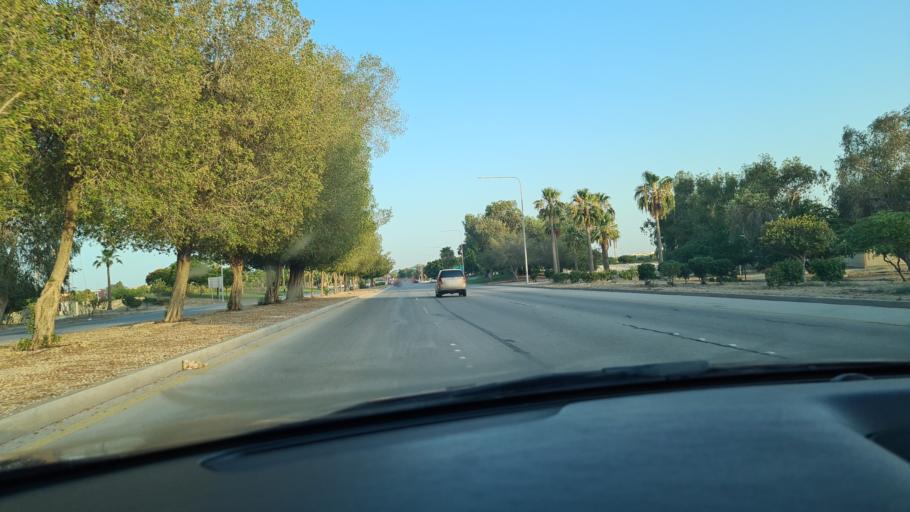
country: SA
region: Eastern Province
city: Al Jubayl
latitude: 27.1282
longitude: 49.5627
